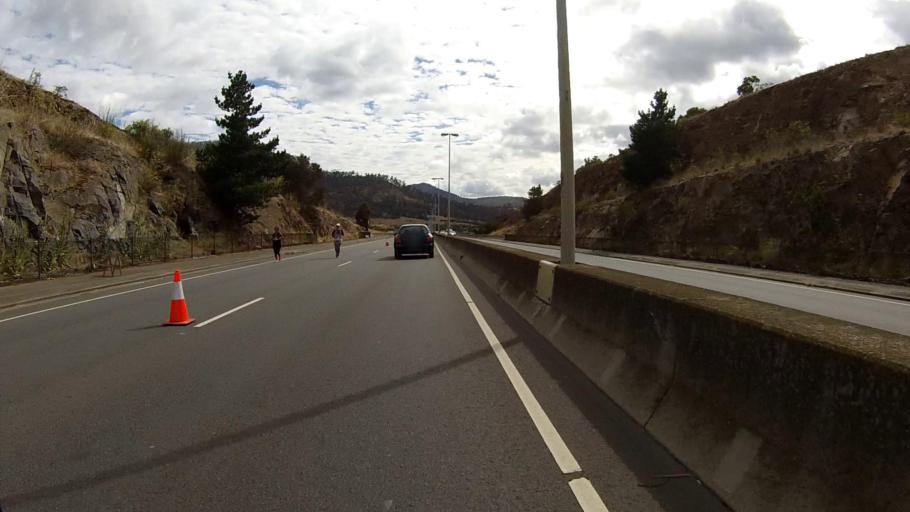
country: AU
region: Tasmania
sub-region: Glenorchy
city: Goodwood
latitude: -42.8219
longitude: 147.3021
